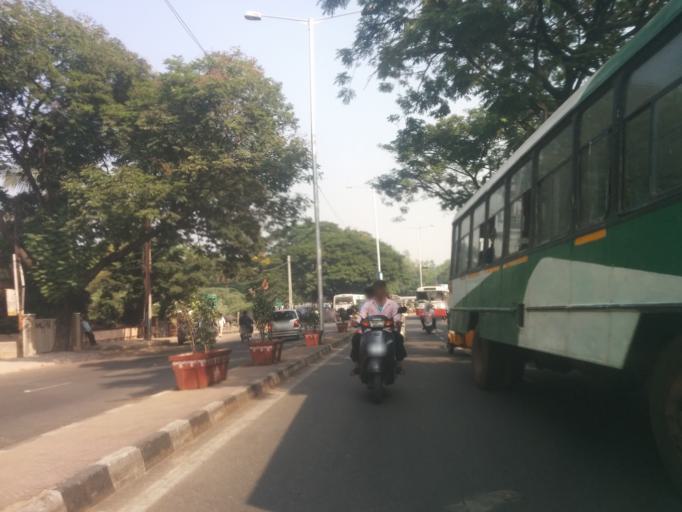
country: IN
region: Telangana
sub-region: Hyderabad
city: Hyderabad
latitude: 17.3949
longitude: 78.4273
